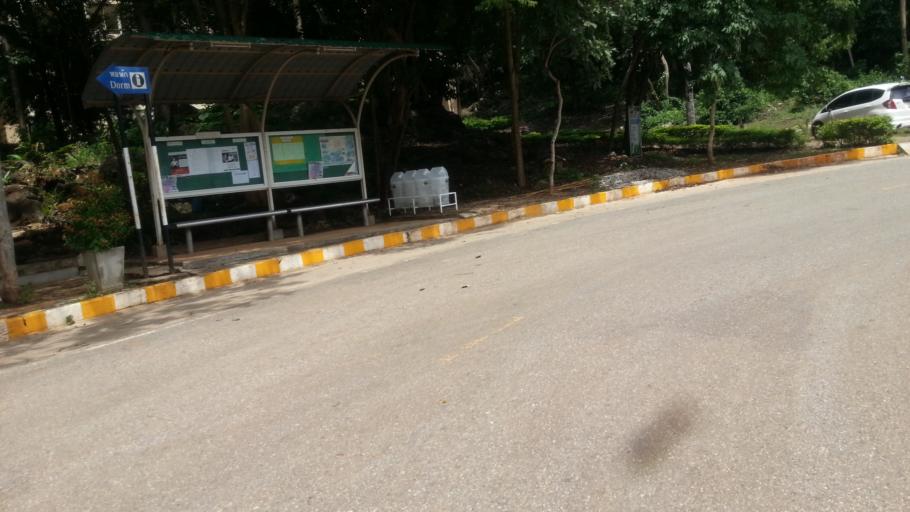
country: TH
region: Kanchanaburi
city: Sai Yok
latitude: 14.1237
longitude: 99.1537
